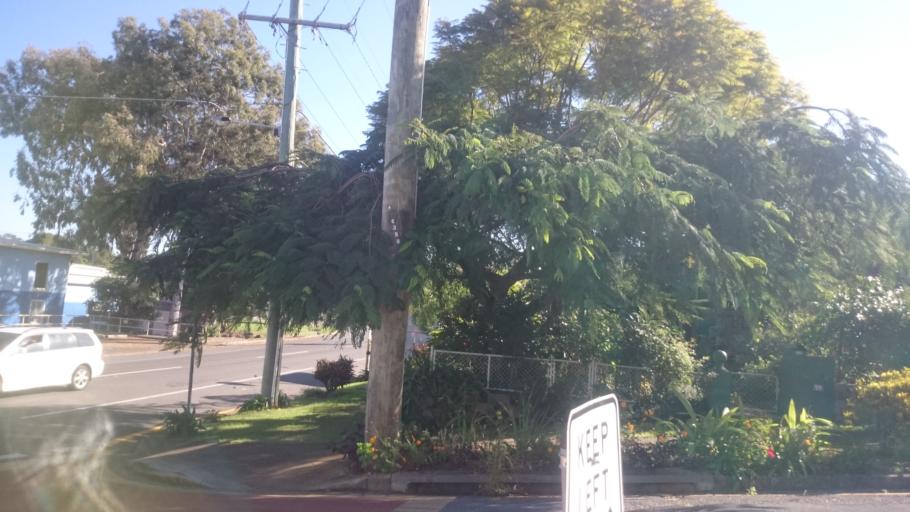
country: AU
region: Queensland
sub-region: Brisbane
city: Manly West
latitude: -27.4670
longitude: 153.1899
